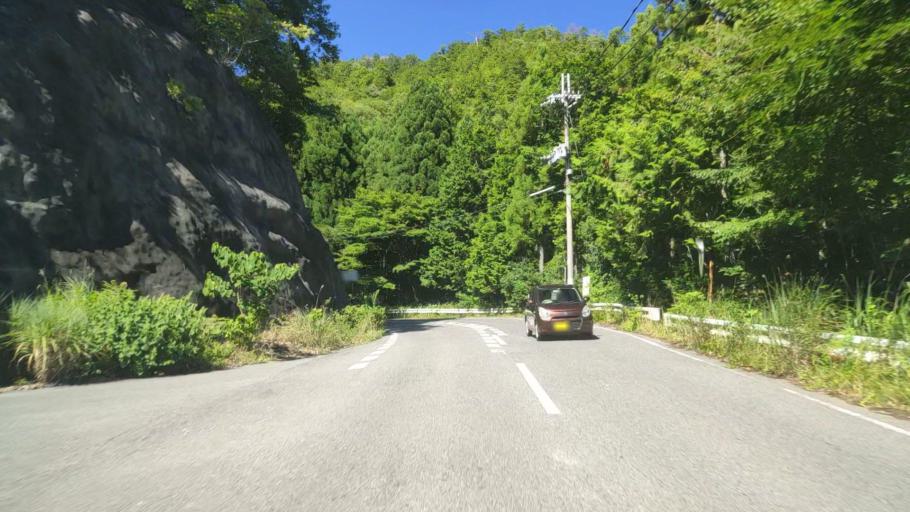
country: JP
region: Nara
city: Yoshino-cho
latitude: 34.4277
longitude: 135.9387
